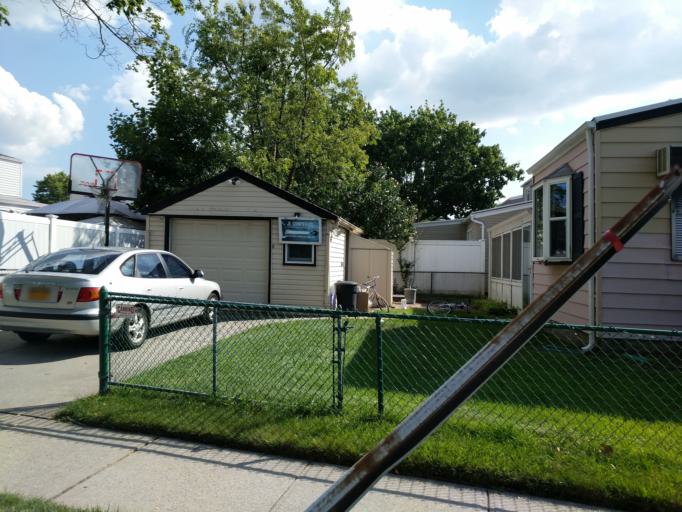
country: US
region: New York
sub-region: Nassau County
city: Hewlett
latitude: 40.6515
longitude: -73.6924
